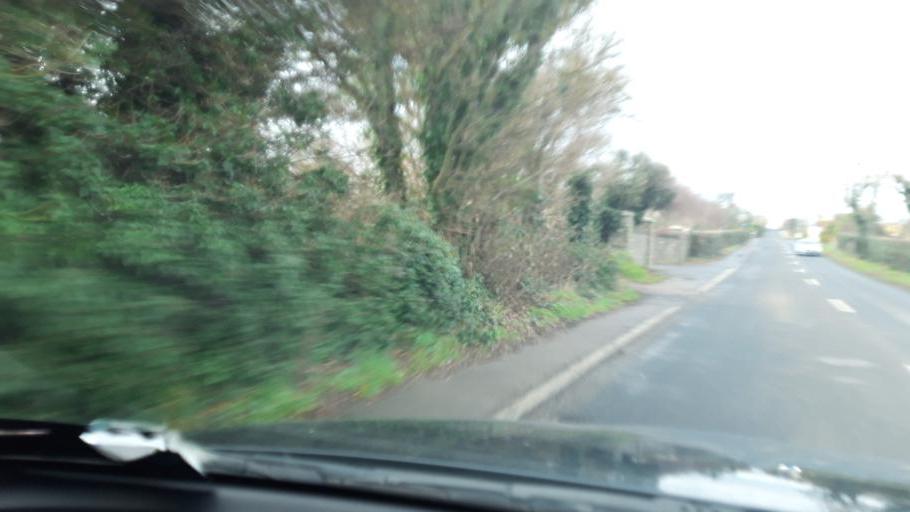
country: IE
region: Leinster
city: An Ros
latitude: 53.5415
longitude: -6.0952
